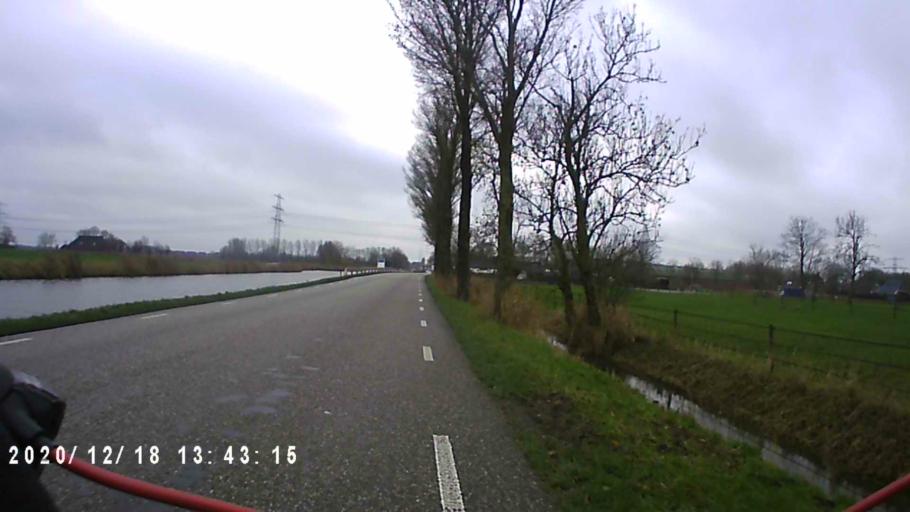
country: NL
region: Groningen
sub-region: Gemeente Bedum
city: Bedum
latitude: 53.3160
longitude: 6.5977
